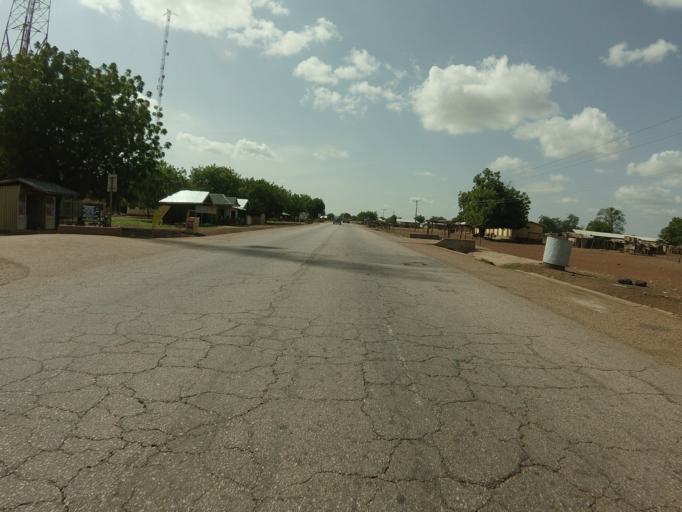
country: GH
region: Northern
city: Savelugu
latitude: 9.8716
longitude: -0.8718
